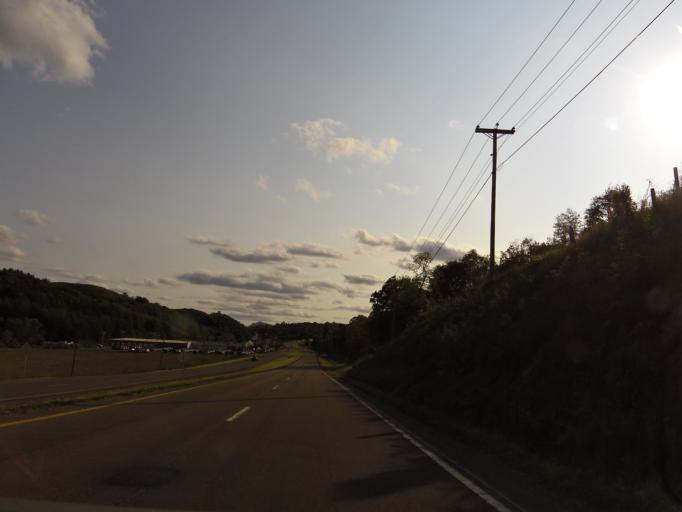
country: US
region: Virginia
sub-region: Tazewell County
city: Tazewell
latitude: 37.1554
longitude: -81.4768
